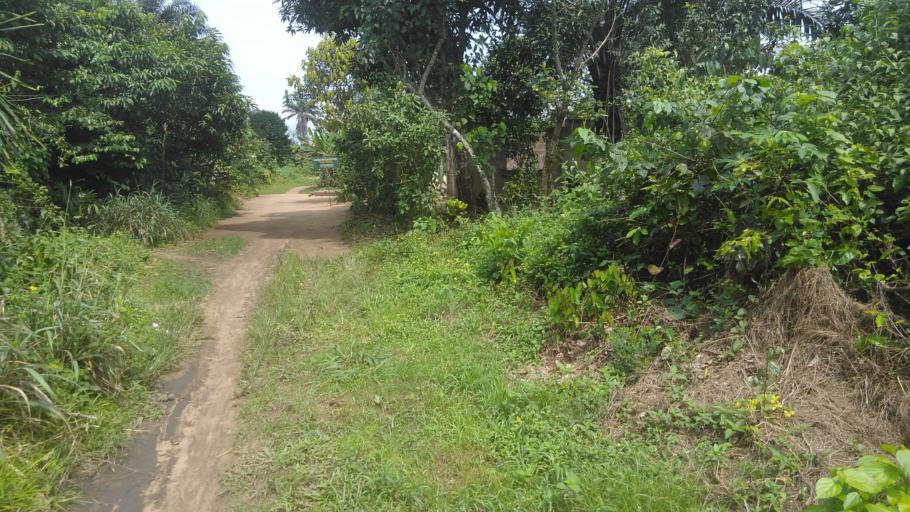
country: NG
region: Abia
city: Aba
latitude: 5.0469
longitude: 7.2500
